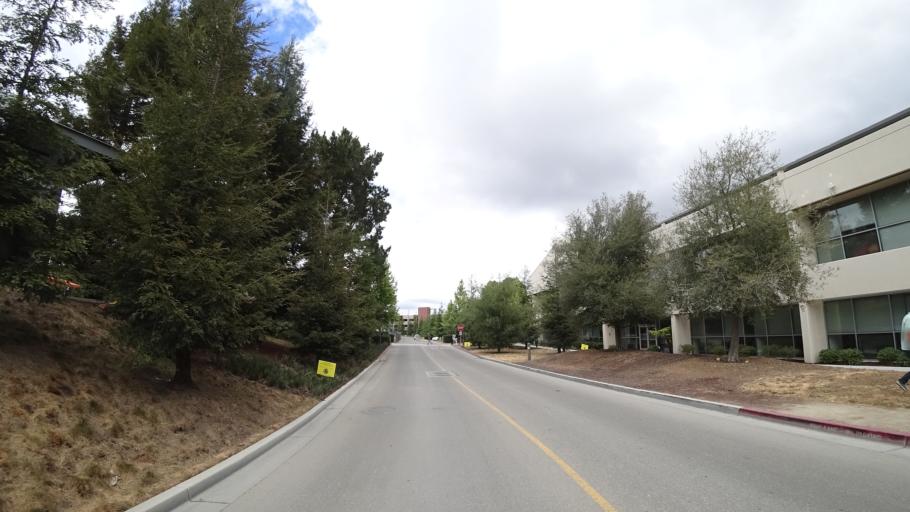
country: US
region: California
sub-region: Santa Clara County
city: Los Altos Hills
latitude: 37.3981
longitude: -122.1386
